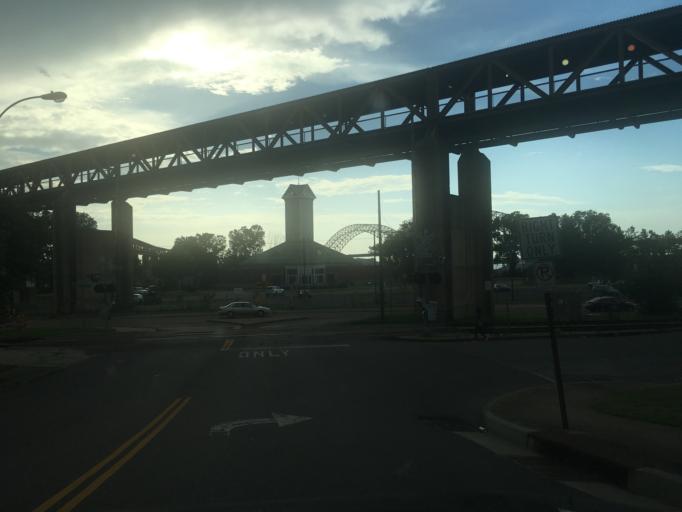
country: US
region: Tennessee
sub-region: Shelby County
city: Memphis
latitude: 35.1486
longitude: -90.0532
